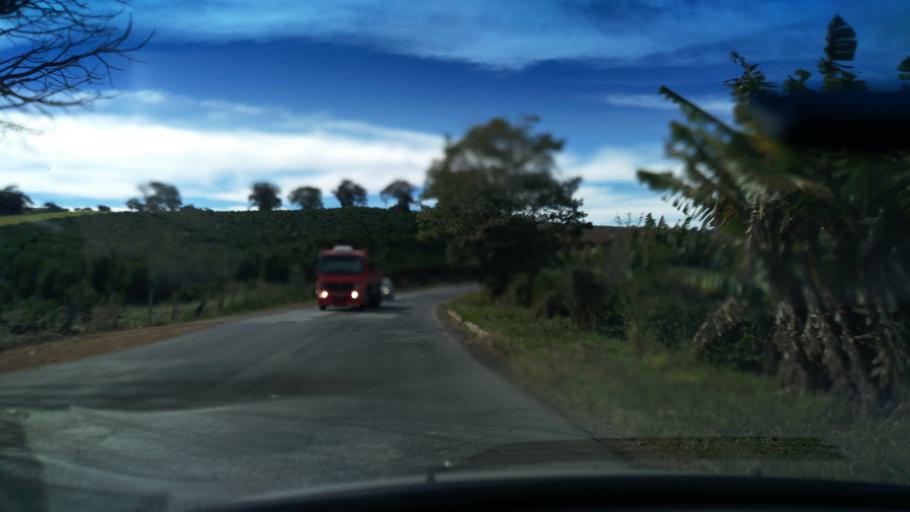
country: BR
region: Minas Gerais
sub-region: Andradas
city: Andradas
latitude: -22.0615
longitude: -46.3849
